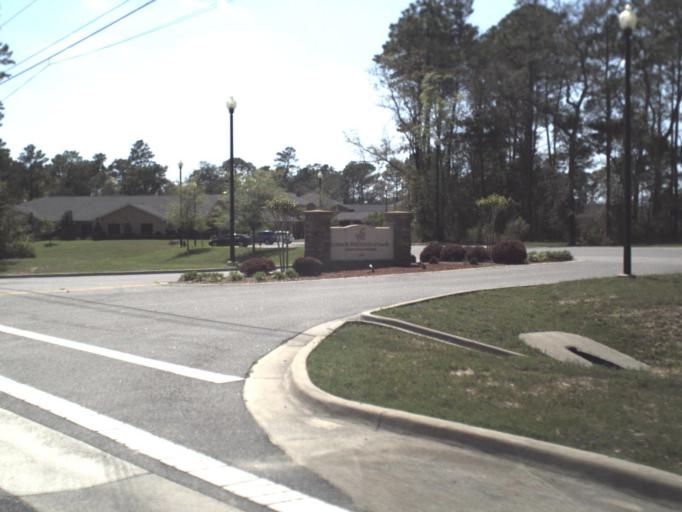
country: US
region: Florida
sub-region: Okaloosa County
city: Niceville
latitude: 30.5312
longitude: -86.4601
